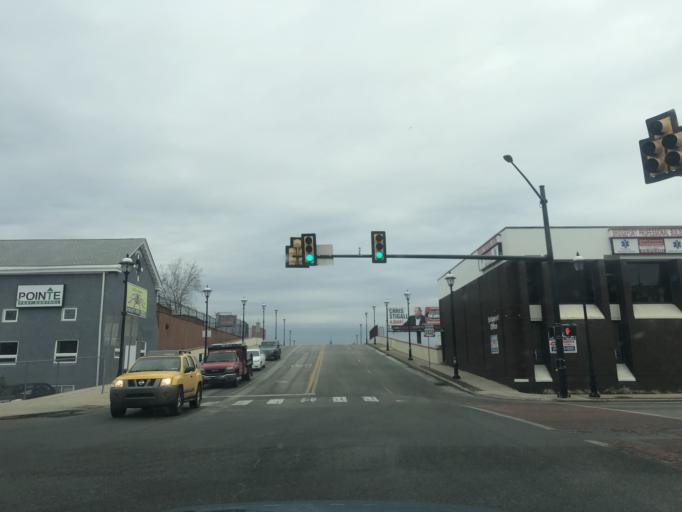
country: US
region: Pennsylvania
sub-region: Montgomery County
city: Bridgeport
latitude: 40.1057
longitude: -75.3468
